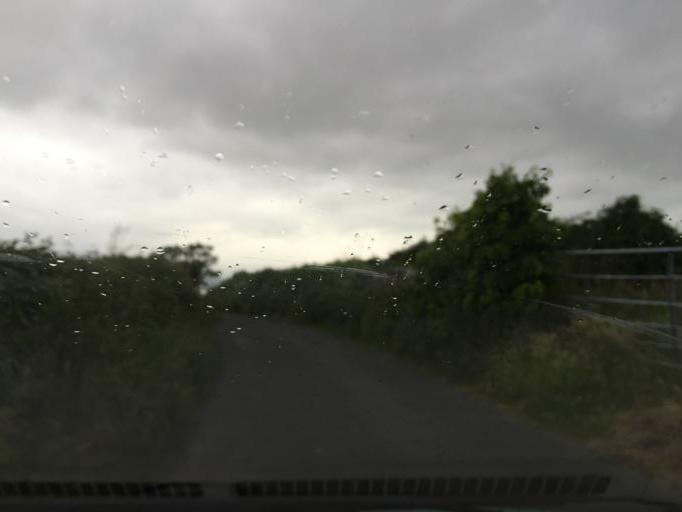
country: IE
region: Connaught
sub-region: Sligo
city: Strandhill
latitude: 54.2493
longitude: -8.5646
